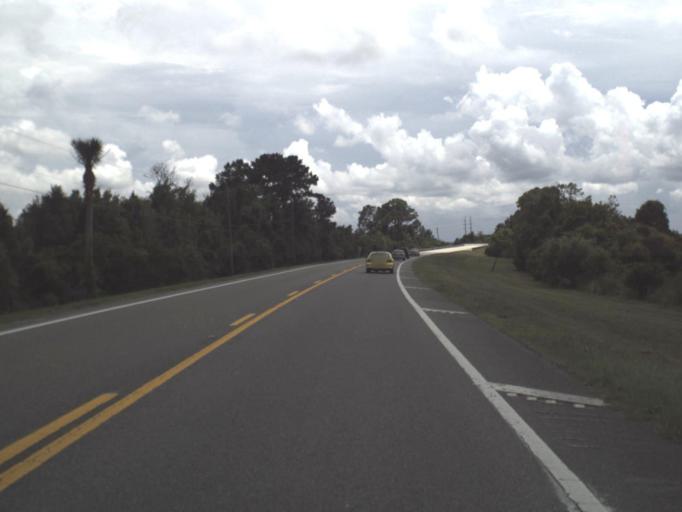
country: US
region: Florida
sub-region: Nassau County
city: Yulee
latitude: 30.5880
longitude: -81.6003
